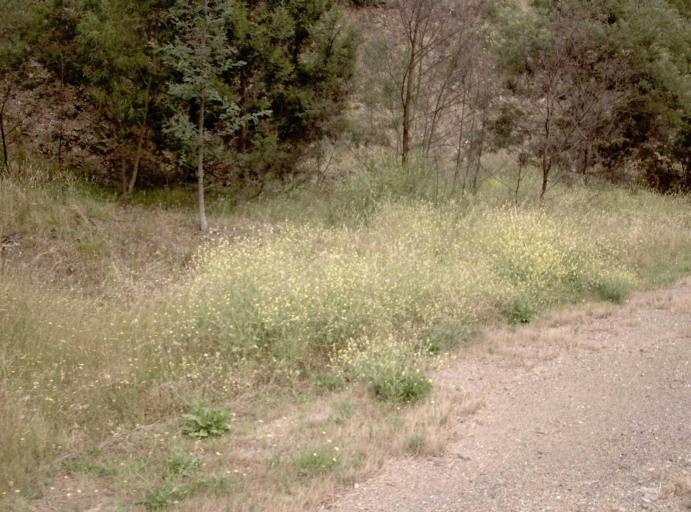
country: AU
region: Victoria
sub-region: Wellington
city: Heyfield
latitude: -37.7752
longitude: 146.6667
